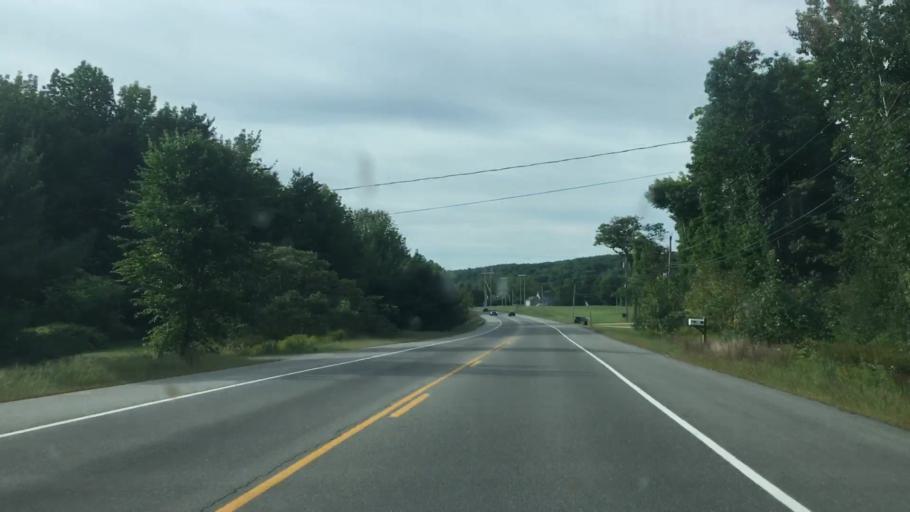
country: US
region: Maine
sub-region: Cumberland County
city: Cumberland Center
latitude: 43.7630
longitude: -70.3012
